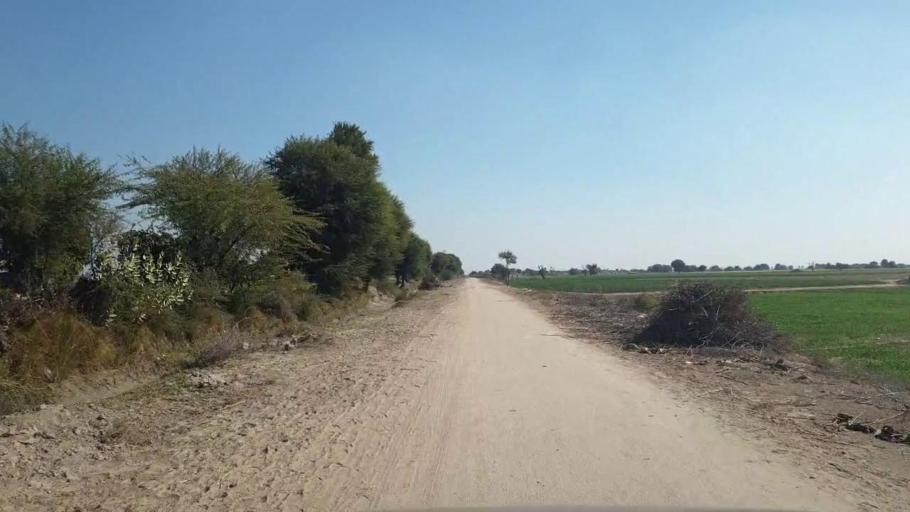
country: PK
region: Sindh
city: Shahpur Chakar
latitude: 26.1400
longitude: 68.6570
